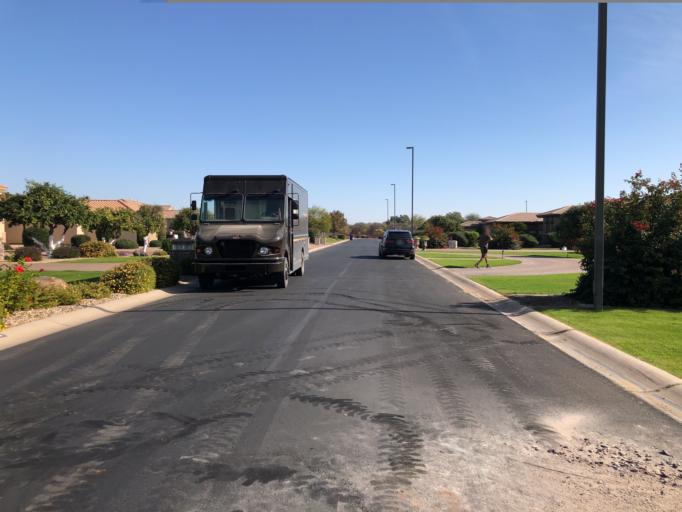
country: US
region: Arizona
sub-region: Maricopa County
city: Queen Creek
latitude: 33.2292
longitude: -111.6902
